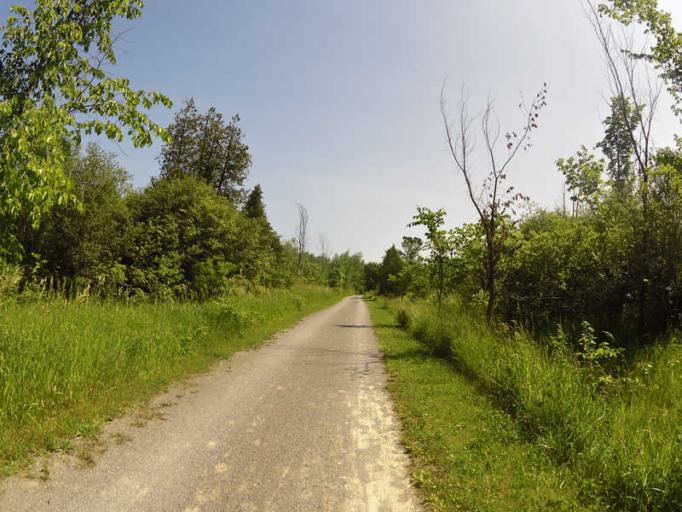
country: CA
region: Ontario
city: Peterborough
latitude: 44.3779
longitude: -78.2795
